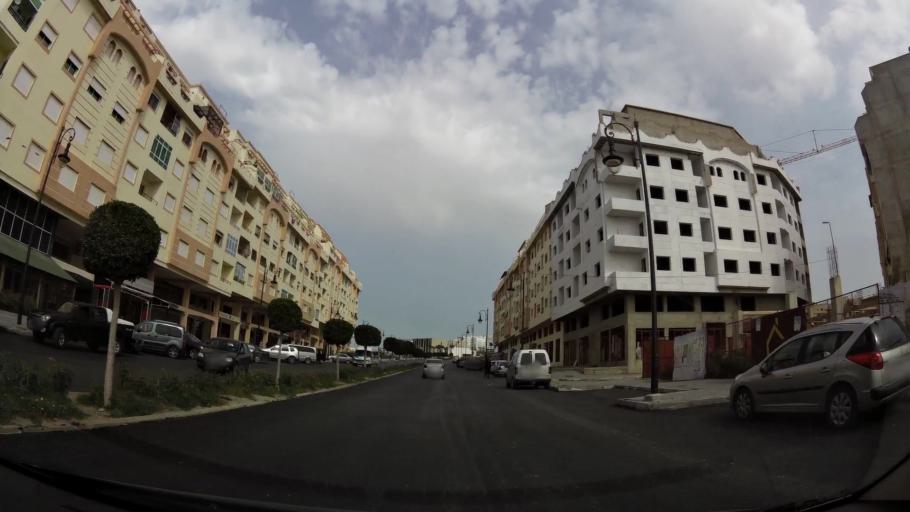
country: MA
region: Tanger-Tetouan
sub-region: Tanger-Assilah
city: Boukhalef
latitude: 35.7372
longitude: -5.8808
